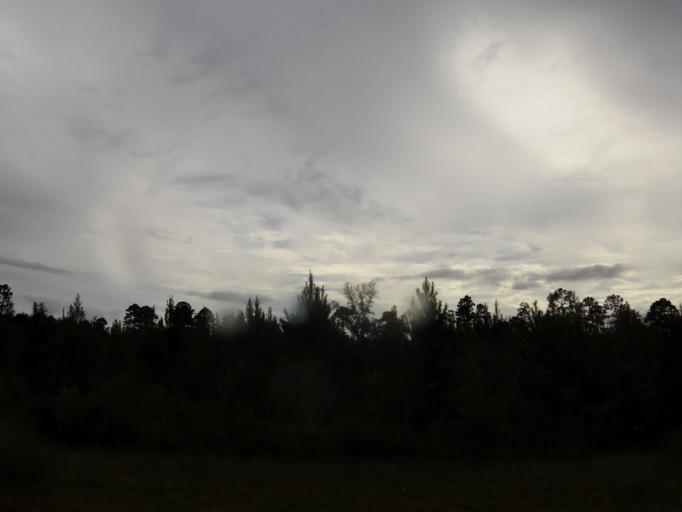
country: US
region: Georgia
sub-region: Wayne County
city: Jesup
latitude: 31.5460
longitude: -81.8624
